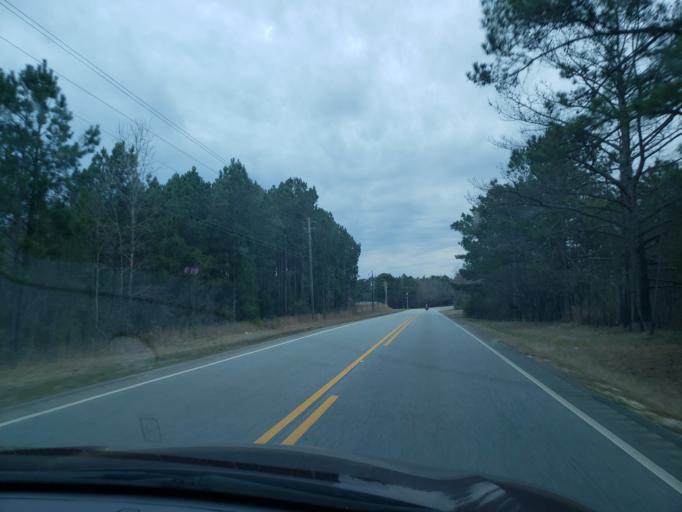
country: US
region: Alabama
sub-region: Chambers County
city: Lafayette
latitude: 33.0047
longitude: -85.3704
